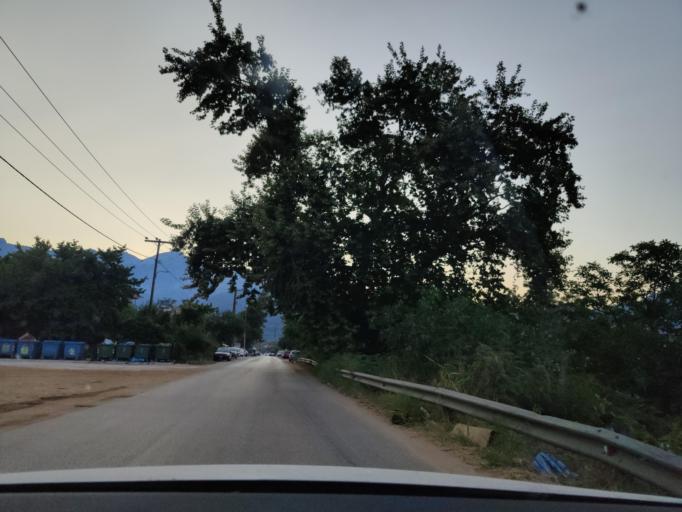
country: GR
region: East Macedonia and Thrace
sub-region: Nomos Kavalas
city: Potamia
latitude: 40.7074
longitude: 24.7590
